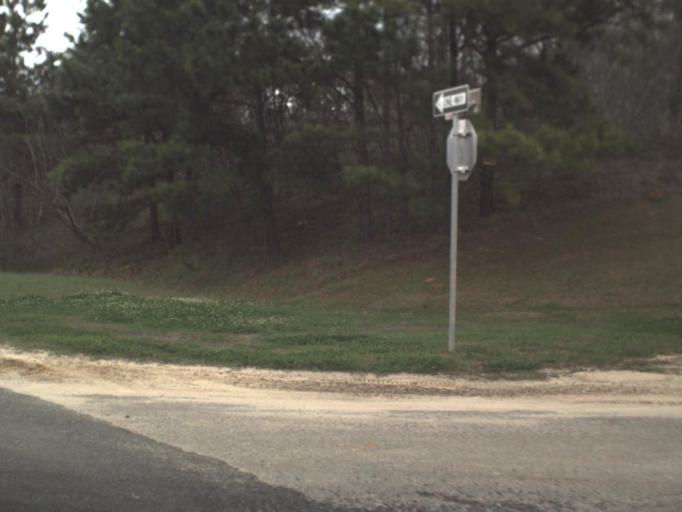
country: US
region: Florida
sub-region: Leon County
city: Tallahassee
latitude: 30.6342
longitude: -84.1688
